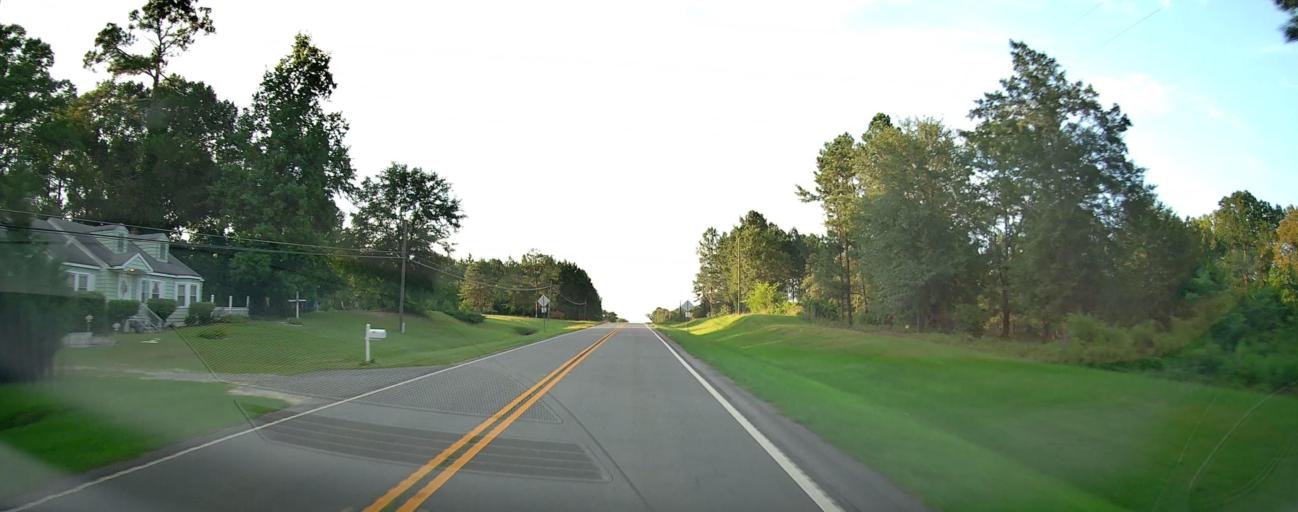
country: US
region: Georgia
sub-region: Taylor County
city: Reynolds
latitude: 32.5780
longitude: -84.0898
